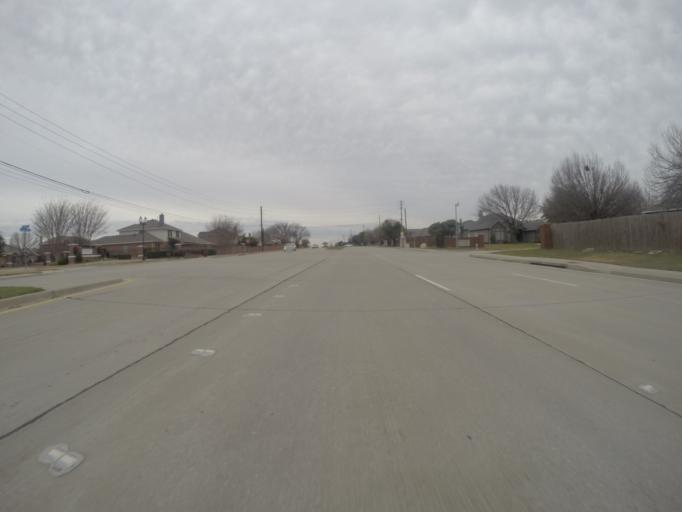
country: US
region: Texas
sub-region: Dallas County
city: Sachse
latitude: 33.0029
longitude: -96.5780
